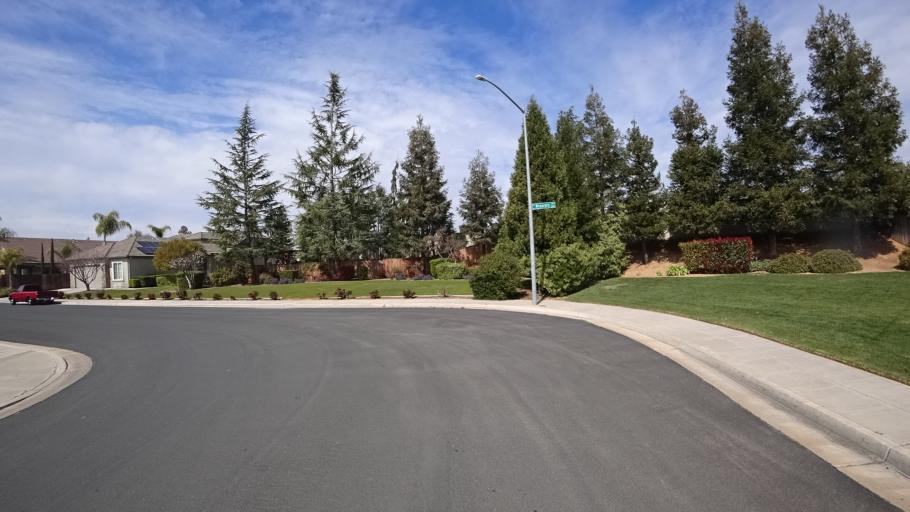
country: US
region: California
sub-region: Fresno County
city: Biola
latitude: 36.8425
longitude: -119.8951
